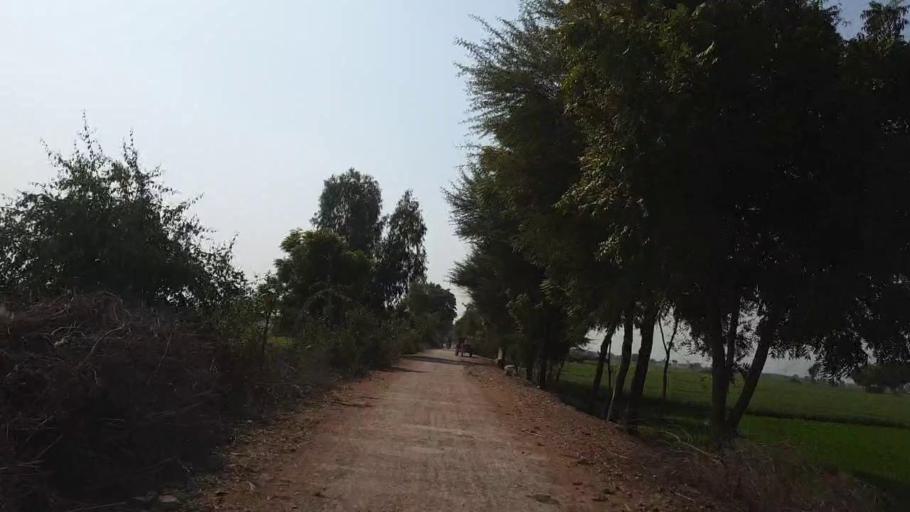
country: PK
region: Sindh
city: Bhit Shah
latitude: 25.7526
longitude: 68.4676
